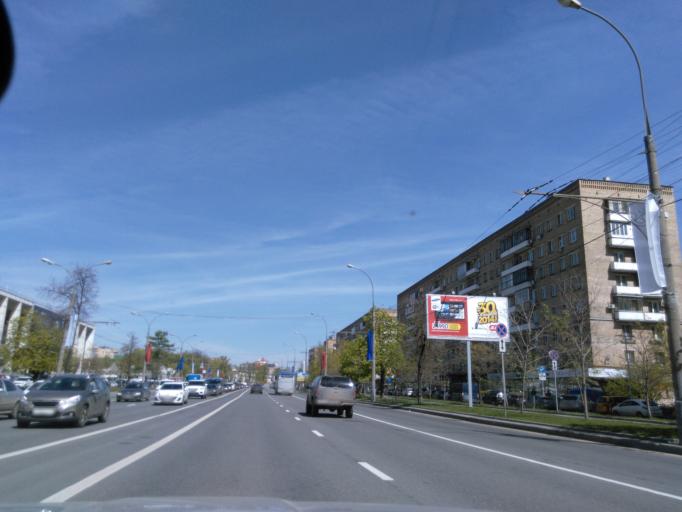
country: RU
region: Moscow
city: Novyye Cheremushki
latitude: 55.7251
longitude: 37.5794
